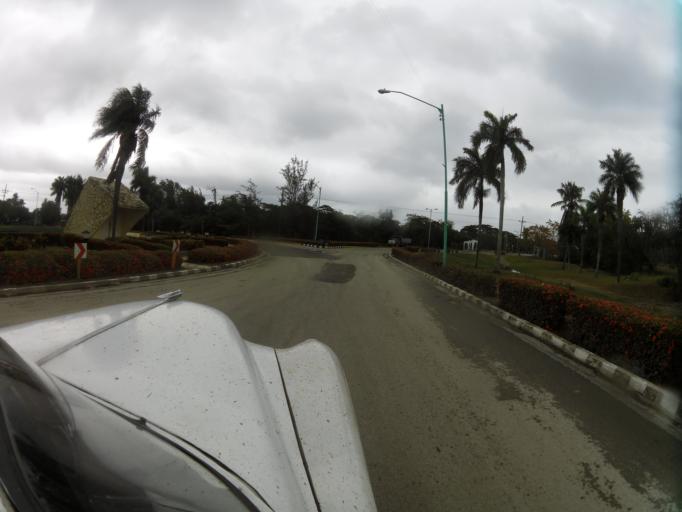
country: CU
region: Las Tunas
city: Las Tunas
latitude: 20.9458
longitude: -76.9415
